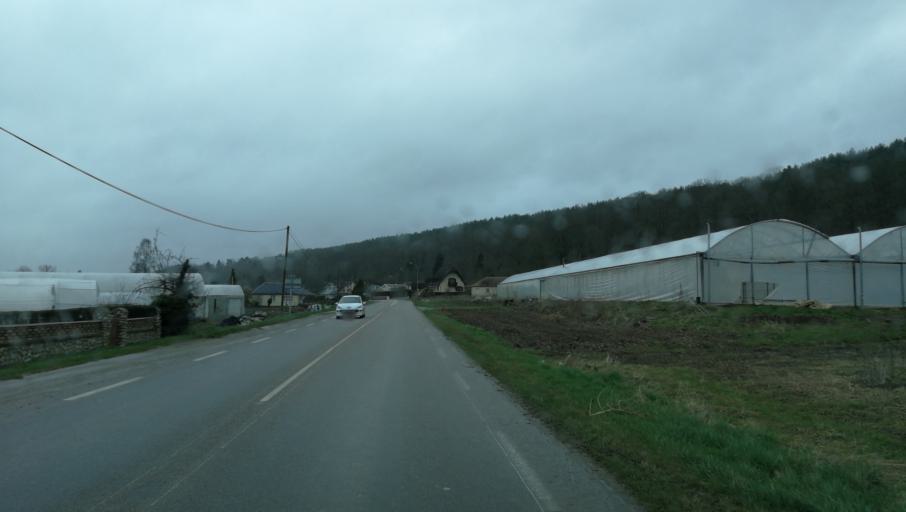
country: FR
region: Haute-Normandie
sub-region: Departement de l'Eure
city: Brionne
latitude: 49.1773
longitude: 0.7251
